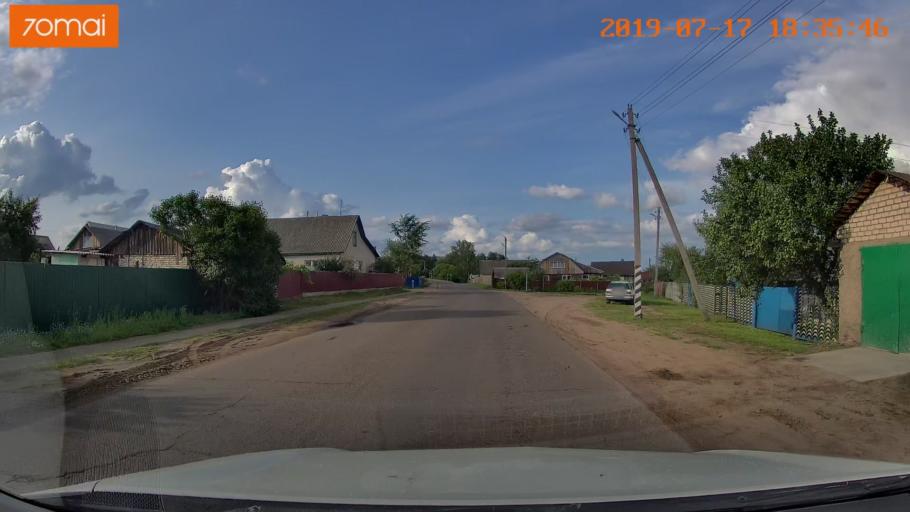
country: BY
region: Mogilev
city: Asipovichy
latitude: 53.2949
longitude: 28.6595
